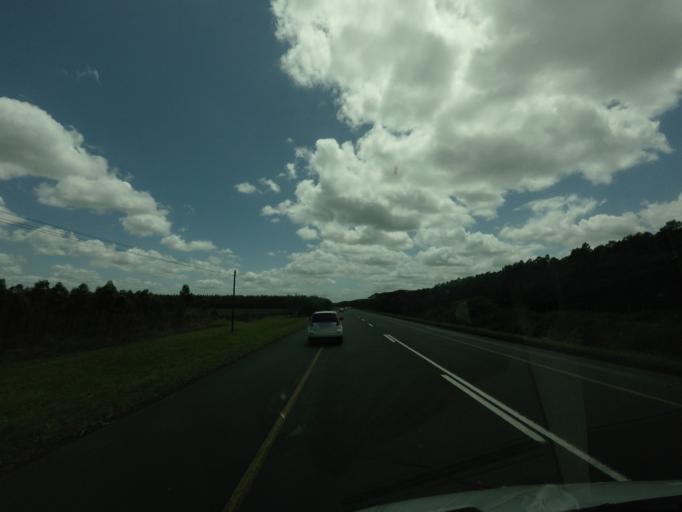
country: ZA
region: KwaZulu-Natal
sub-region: uThungulu District Municipality
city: KwaMbonambi
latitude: -28.5656
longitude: 32.1137
